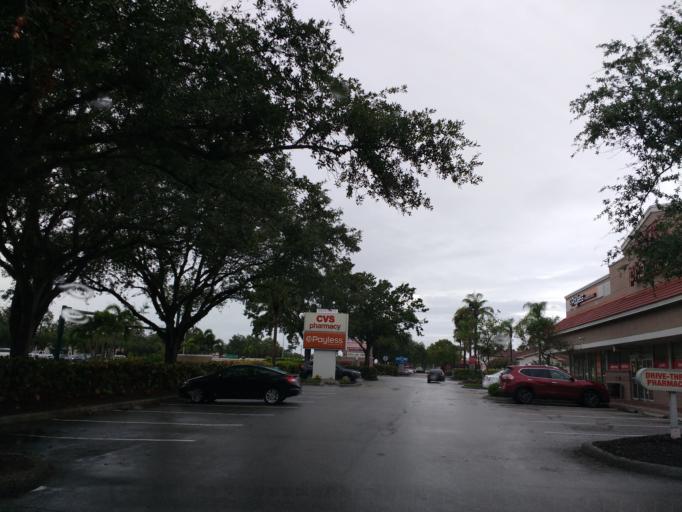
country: US
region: Florida
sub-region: Collier County
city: Pine Ridge
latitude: 26.2083
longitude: -81.7677
